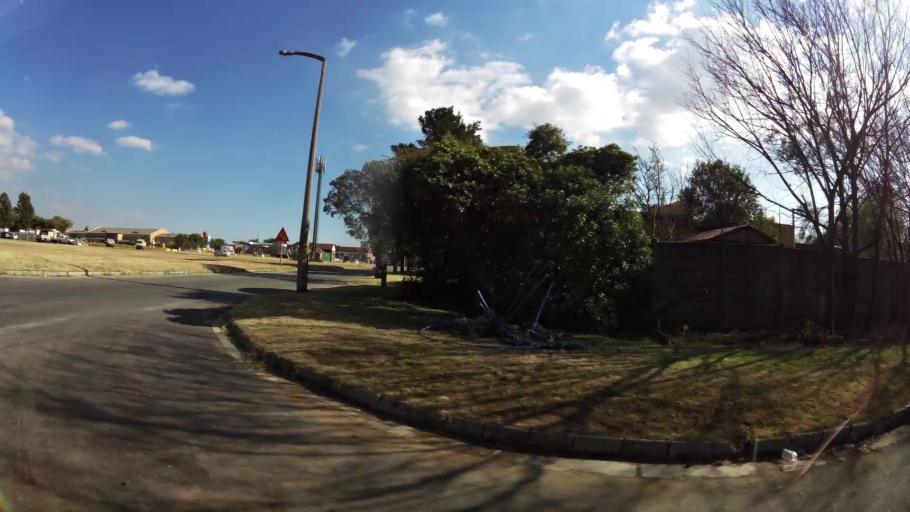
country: ZA
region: Gauteng
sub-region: Ekurhuleni Metropolitan Municipality
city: Benoni
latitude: -26.1451
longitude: 28.3453
